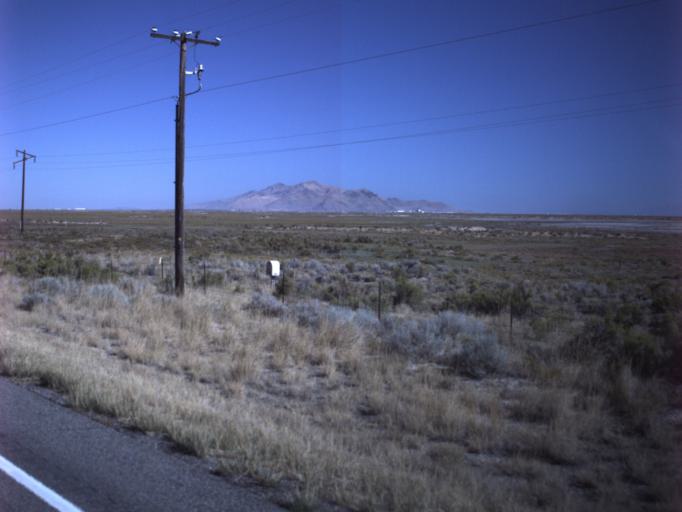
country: US
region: Utah
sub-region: Tooele County
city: Grantsville
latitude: 40.6469
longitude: -112.5289
